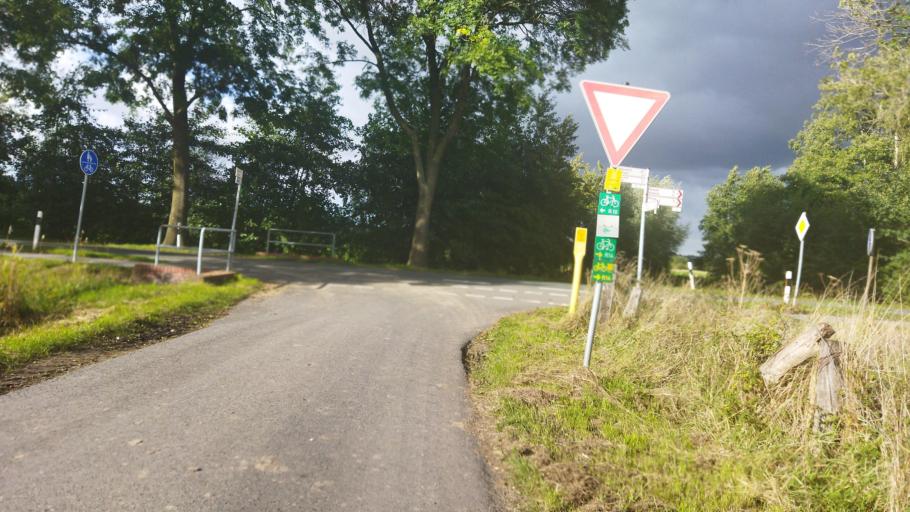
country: DE
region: North Rhine-Westphalia
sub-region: Regierungsbezirk Munster
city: Dulmen
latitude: 51.8949
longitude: 7.2583
